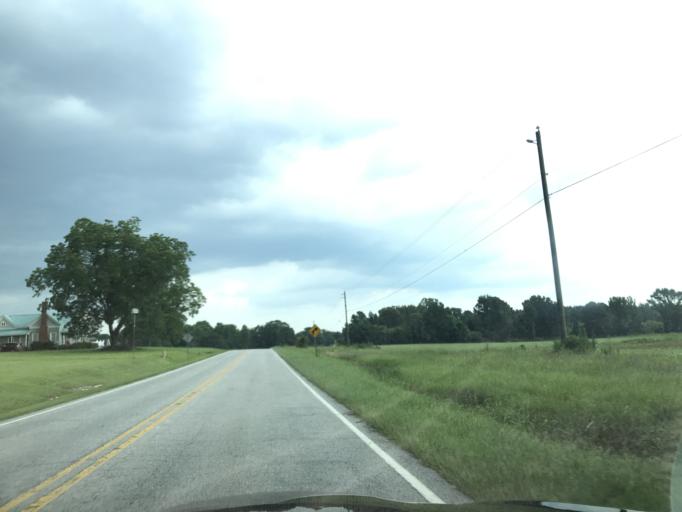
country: US
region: North Carolina
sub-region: Johnston County
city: Four Oaks
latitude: 35.5110
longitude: -78.4771
